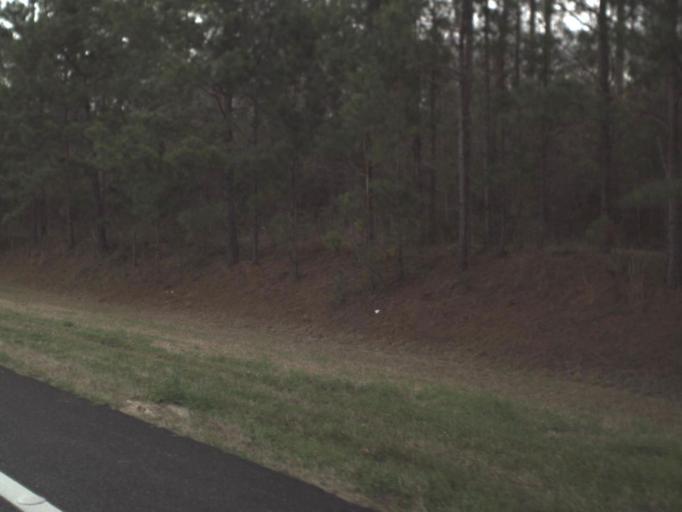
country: US
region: Georgia
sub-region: Grady County
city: Cairo
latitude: 30.6576
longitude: -84.1689
